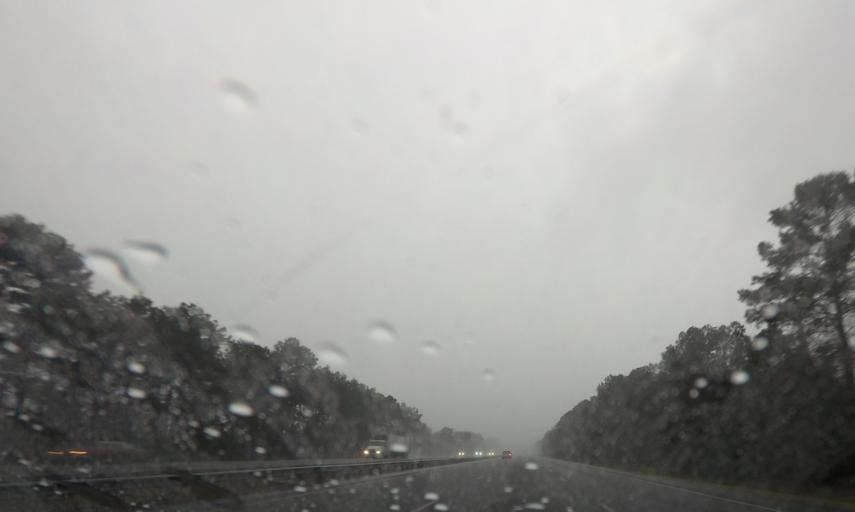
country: US
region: Georgia
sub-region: Lowndes County
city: Valdosta
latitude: 30.7872
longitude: -83.3002
